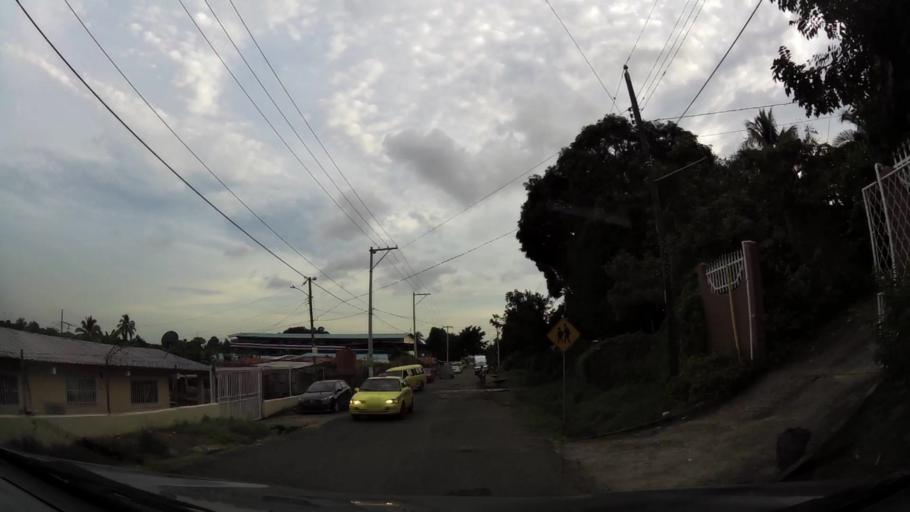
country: PA
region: Panama
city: Tocumen
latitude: 9.0909
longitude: -79.3942
